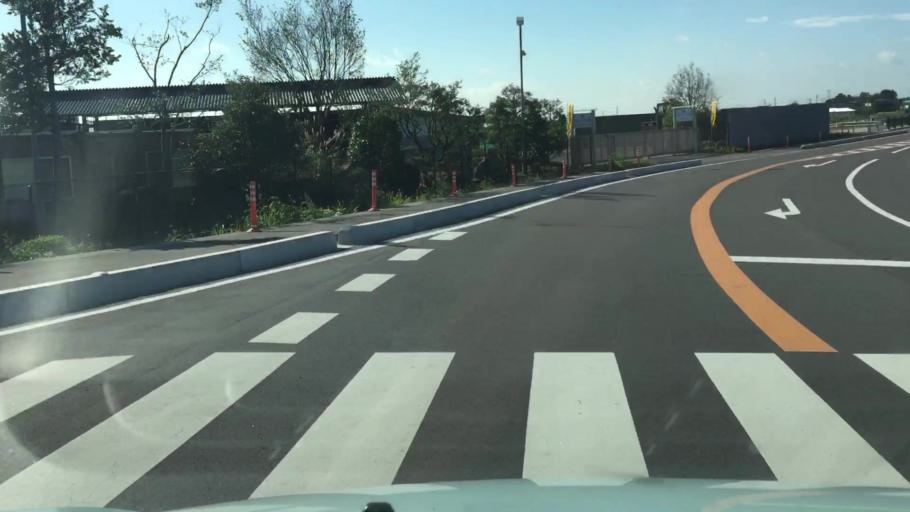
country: JP
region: Tochigi
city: Ujiie
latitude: 36.6559
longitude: 140.0230
